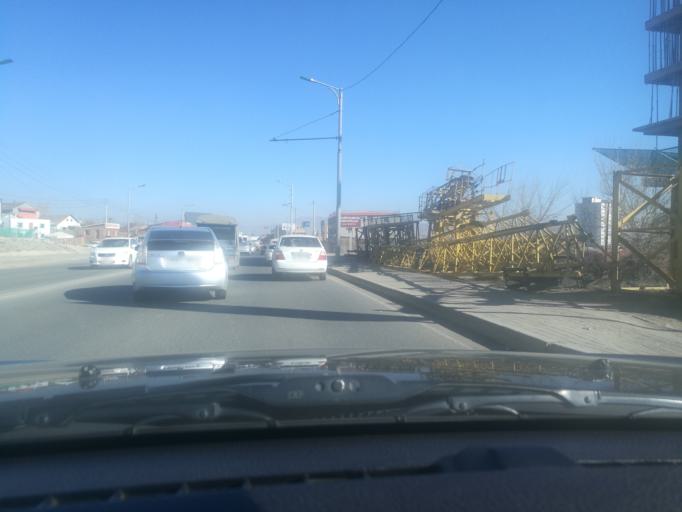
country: MN
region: Ulaanbaatar
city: Ulaanbaatar
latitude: 47.9352
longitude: 106.9077
